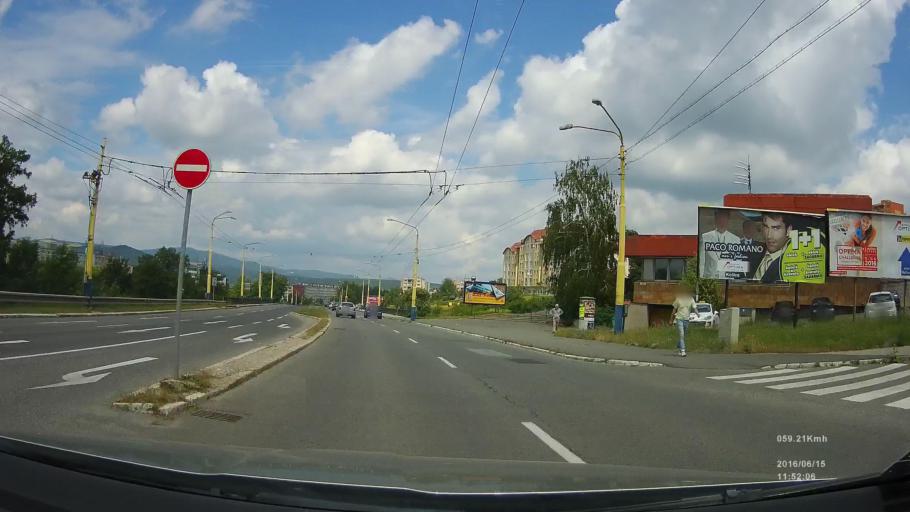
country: SK
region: Kosicky
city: Kosice
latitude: 48.7356
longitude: 21.2845
